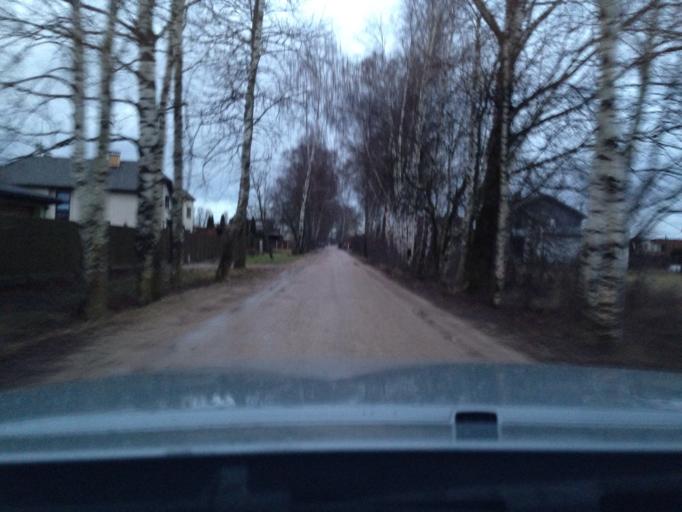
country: LV
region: Marupe
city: Marupe
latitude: 56.9142
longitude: 24.0273
